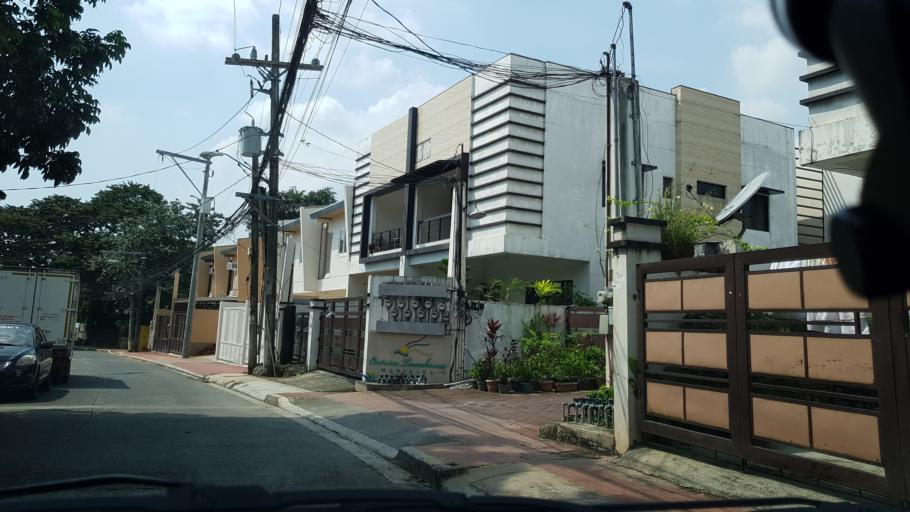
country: PH
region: Calabarzon
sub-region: Province of Rizal
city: Antipolo
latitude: 14.6546
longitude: 121.1191
